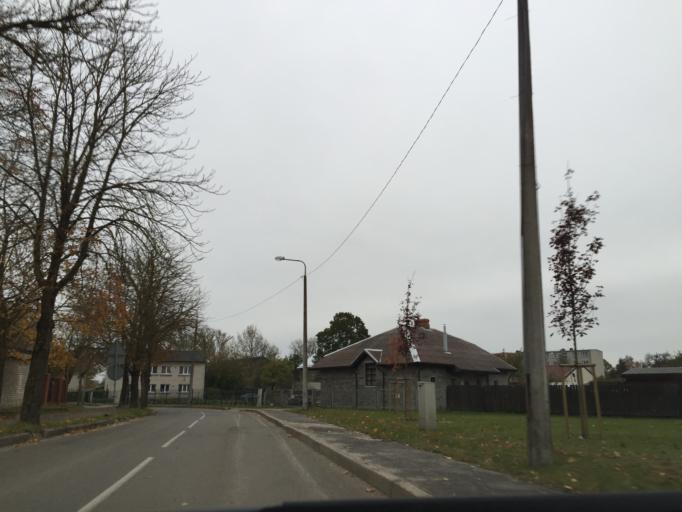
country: LV
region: Jelgava
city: Jelgava
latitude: 56.6476
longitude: 23.7117
